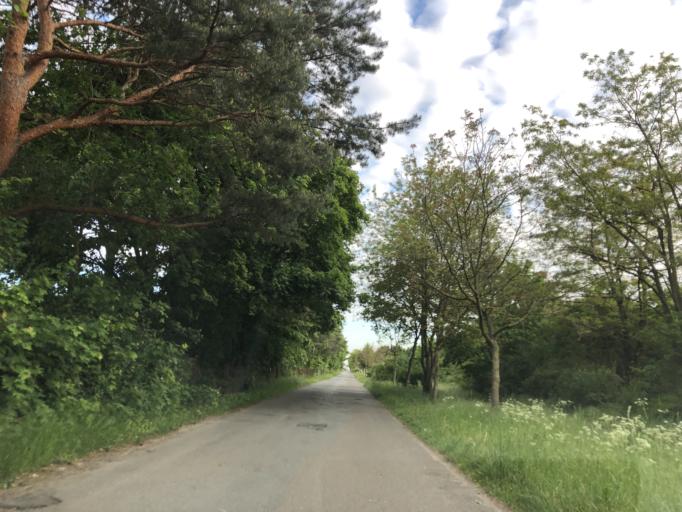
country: DE
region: Hesse
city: Weiterstadt
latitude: 49.9429
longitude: 8.6034
